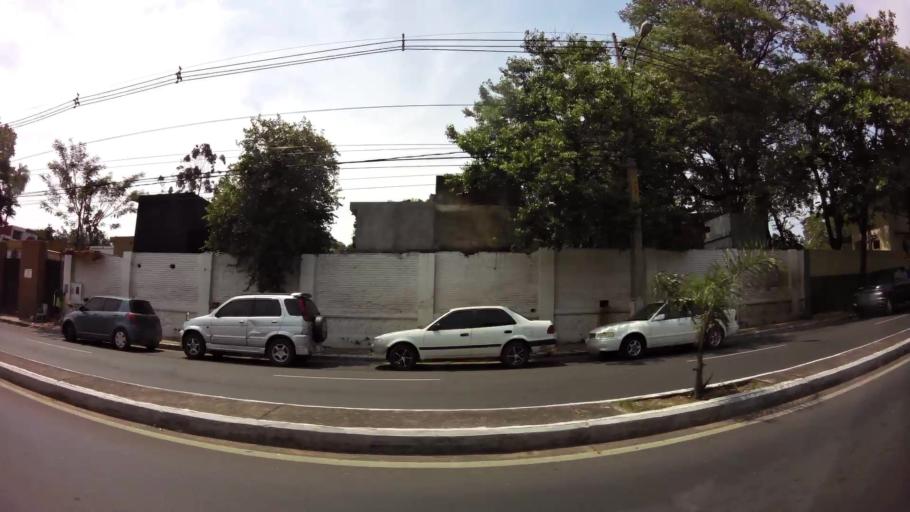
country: PY
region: Asuncion
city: Asuncion
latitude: -25.2932
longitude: -57.5919
